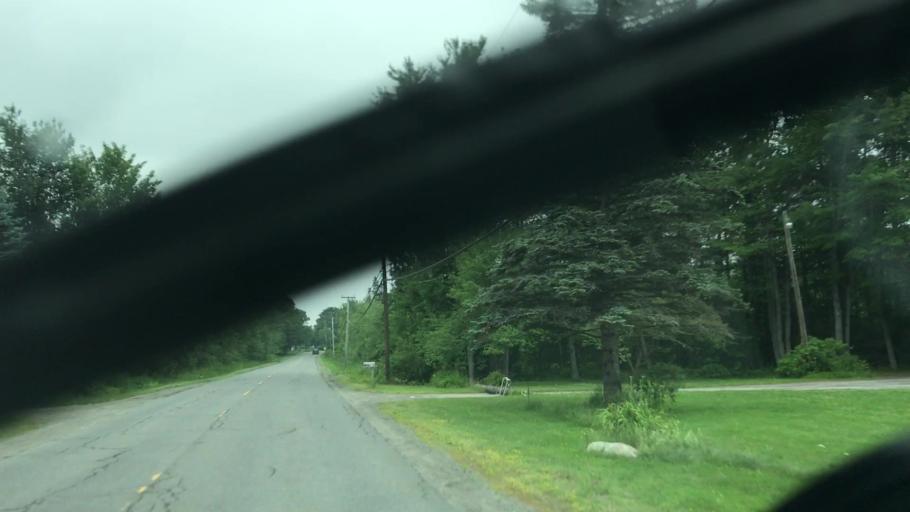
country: US
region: Maine
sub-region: Penobscot County
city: Orono
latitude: 44.8825
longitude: -68.7096
